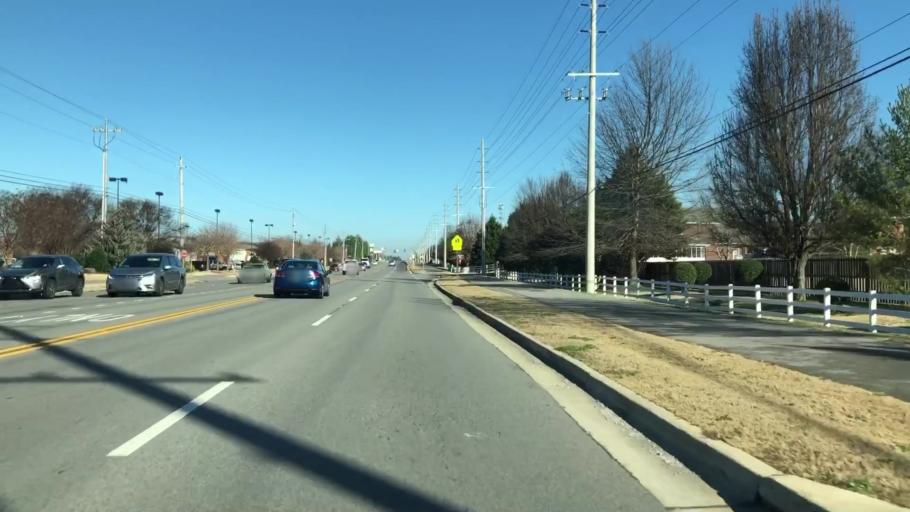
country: US
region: Alabama
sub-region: Madison County
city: Madison
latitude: 34.7293
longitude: -86.7863
